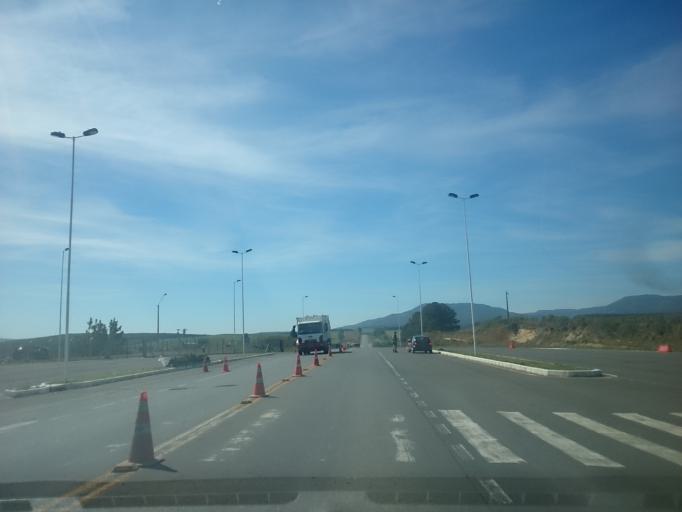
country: BR
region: Santa Catarina
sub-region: Lages
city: Lages
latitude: -27.7697
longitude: -50.1779
